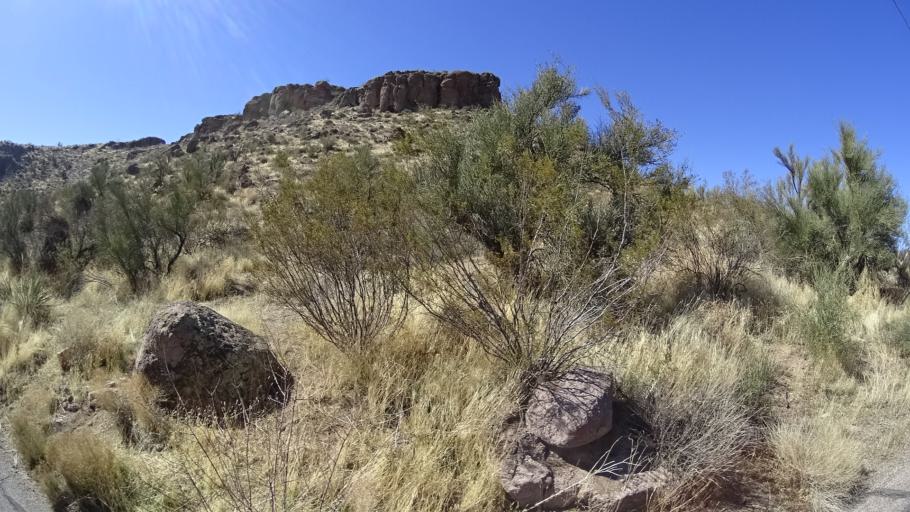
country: US
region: Arizona
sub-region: Mohave County
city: Kingman
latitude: 35.2027
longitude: -114.0616
